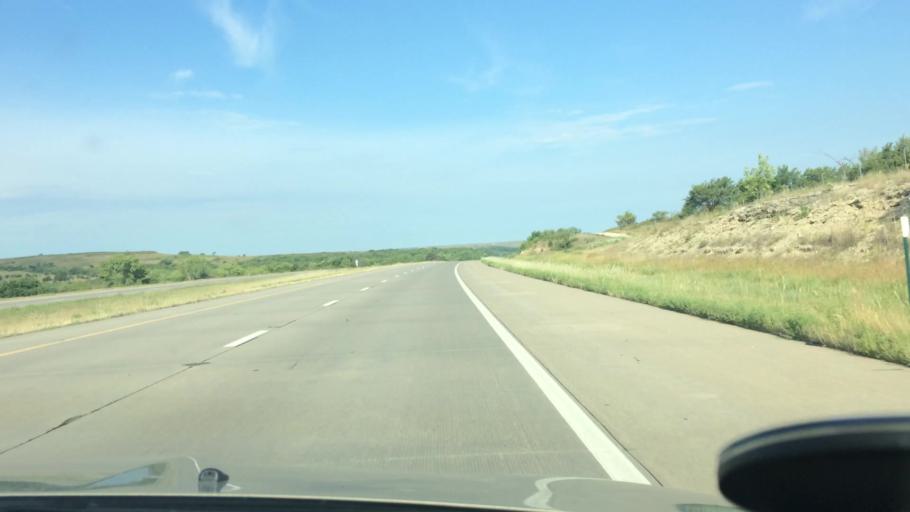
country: US
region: Kansas
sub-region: Wabaunsee County
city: Alma
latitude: 39.0645
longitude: -96.4479
